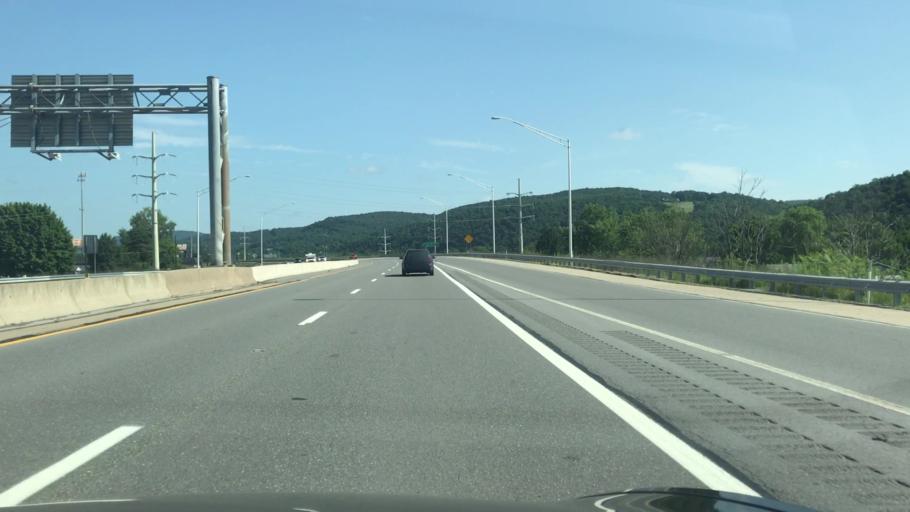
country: US
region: Pennsylvania
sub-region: Lycoming County
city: Garden View
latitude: 41.2525
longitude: -77.0459
